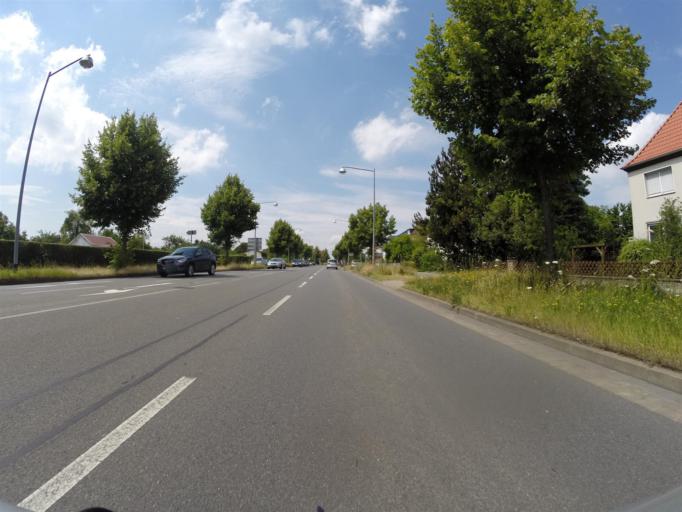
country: DE
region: Lower Saxony
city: Laatzen
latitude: 52.3180
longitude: 9.8051
